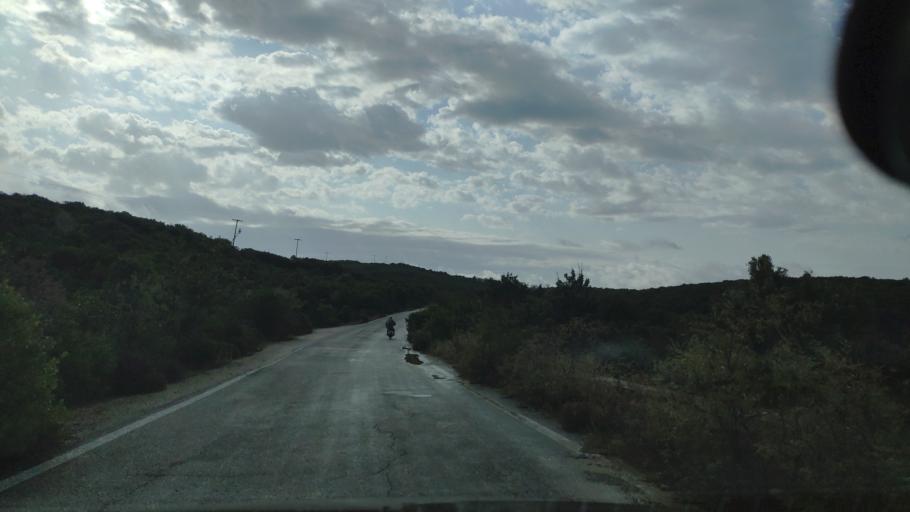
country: GR
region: West Greece
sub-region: Nomos Aitolias kai Akarnanias
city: Sardinia
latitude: 38.8839
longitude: 21.2444
